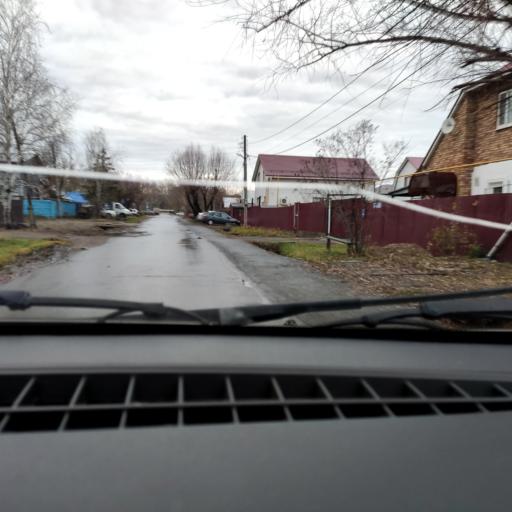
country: RU
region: Bashkortostan
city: Avdon
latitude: 54.6989
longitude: 55.8219
